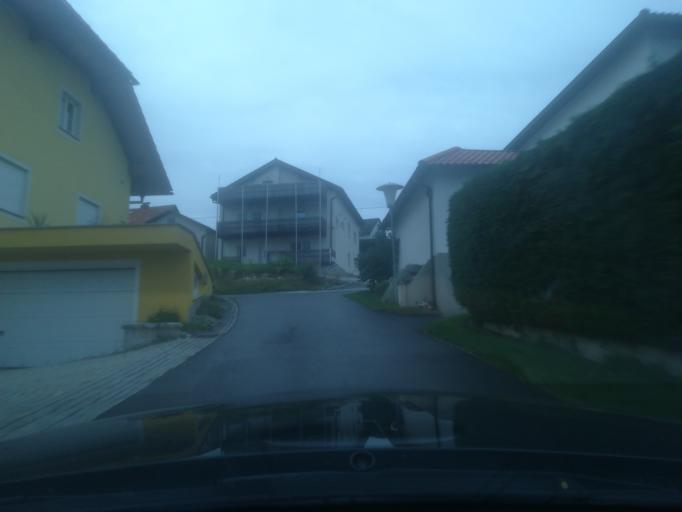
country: AT
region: Upper Austria
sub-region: Politischer Bezirk Urfahr-Umgebung
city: Engerwitzdorf
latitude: 48.3609
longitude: 14.5208
